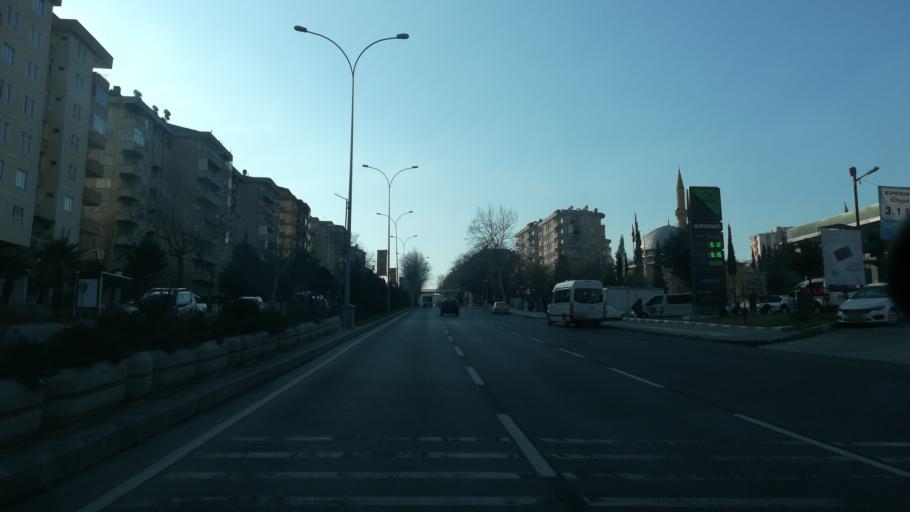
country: TR
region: Kahramanmaras
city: Kahramanmaras
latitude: 37.5840
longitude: 36.9132
